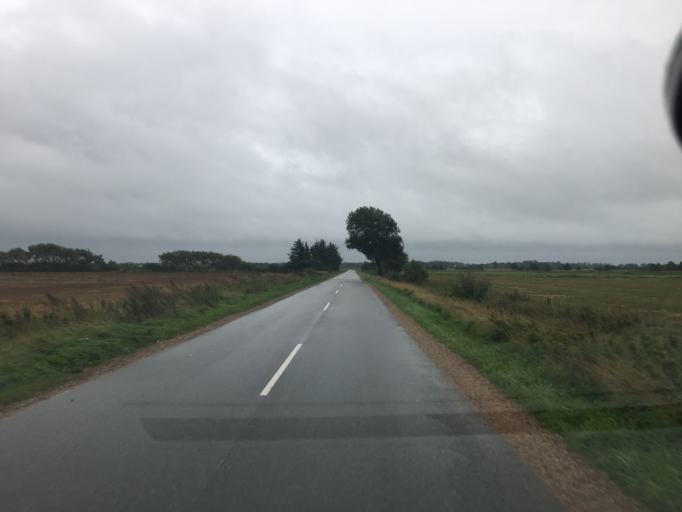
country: DK
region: South Denmark
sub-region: Tonder Kommune
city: Logumkloster
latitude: 54.9738
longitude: 9.0429
